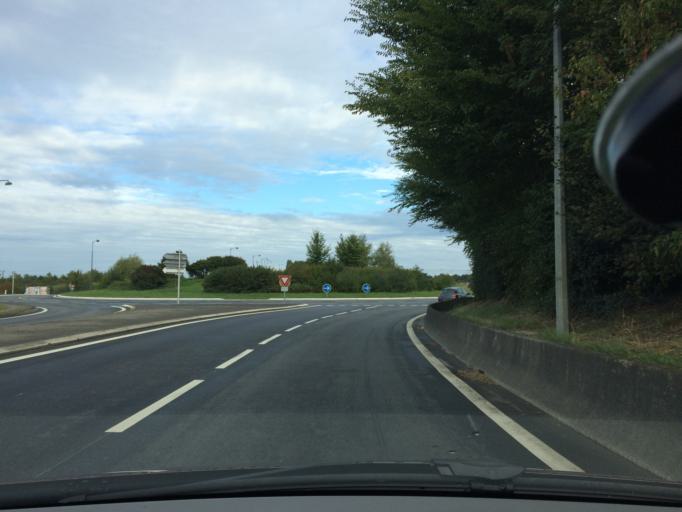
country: FR
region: Brittany
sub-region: Departement d'Ille-et-Vilaine
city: Chantepie
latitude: 48.0818
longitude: -1.6390
